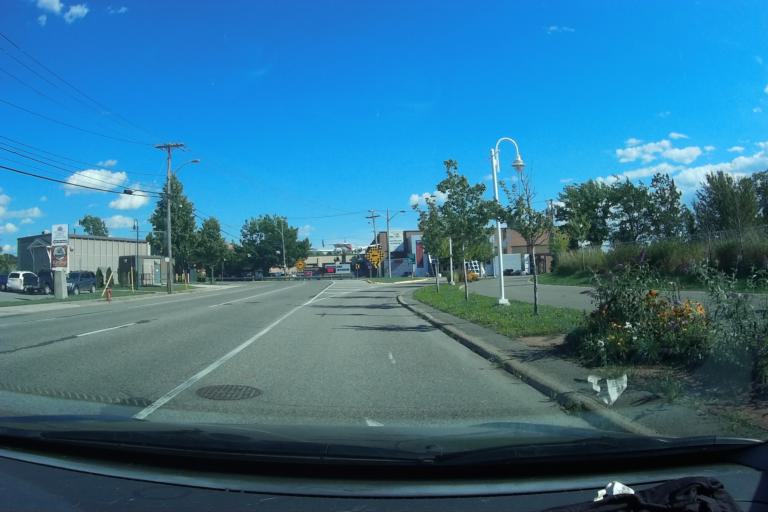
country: CA
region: Ontario
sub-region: Algoma
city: Sault Ste. Marie
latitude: 46.5056
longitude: -84.3259
